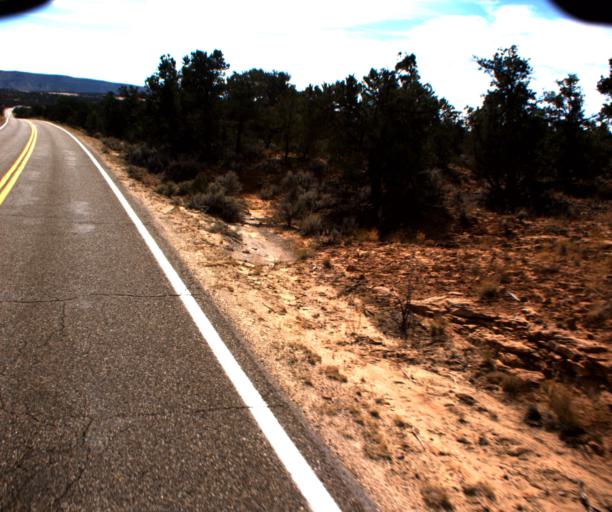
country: US
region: Arizona
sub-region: Navajo County
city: Kayenta
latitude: 36.6201
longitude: -110.5072
